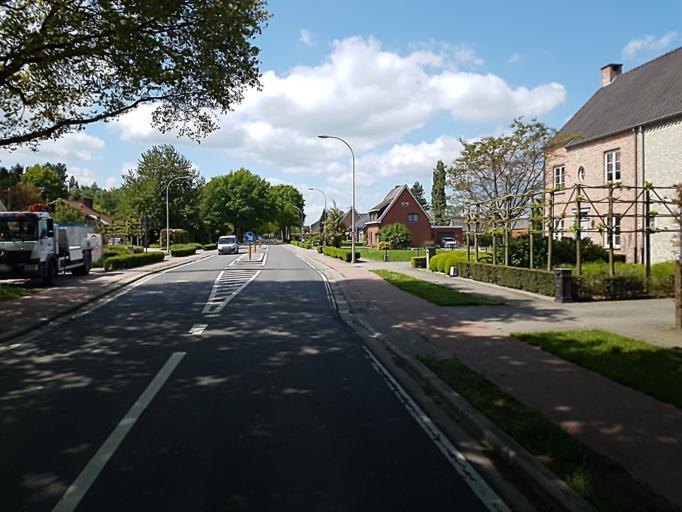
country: BE
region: Flanders
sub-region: Provincie Antwerpen
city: Rijkevorsel
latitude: 51.3485
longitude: 4.7499
